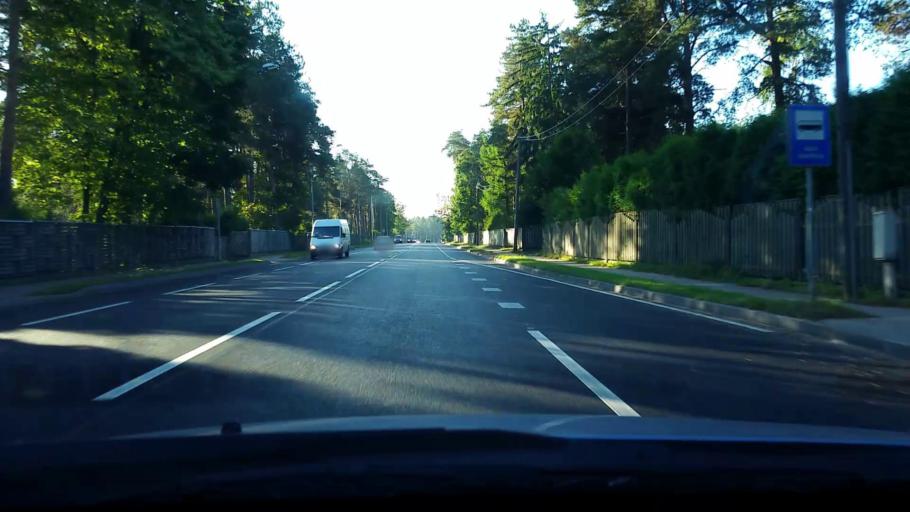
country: LV
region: Adazi
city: Adazi
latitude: 57.0364
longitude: 24.3173
